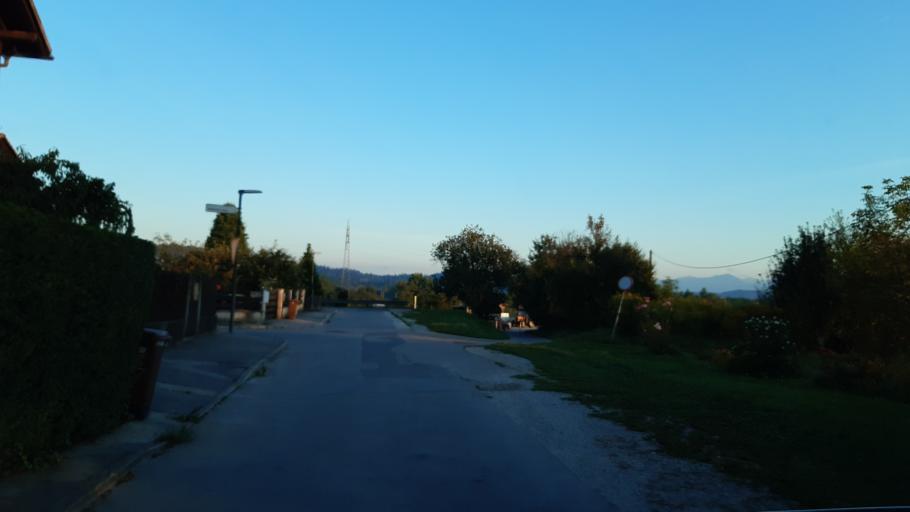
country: SI
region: Medvode
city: Zgornje Pirnice
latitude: 46.1037
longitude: 14.4504
